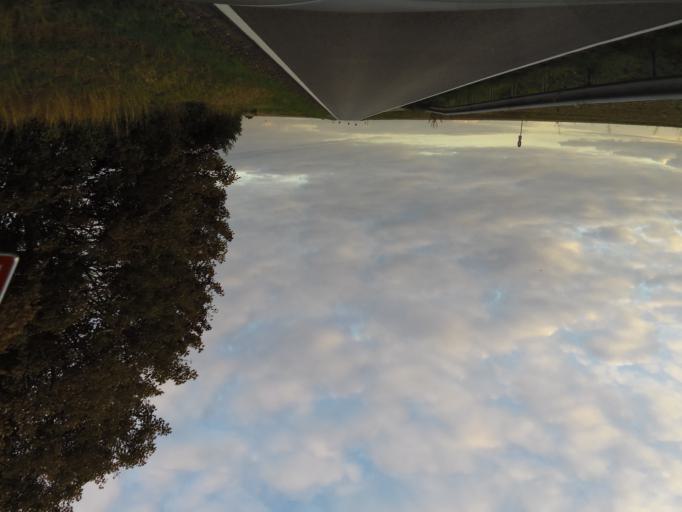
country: DE
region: Rheinland-Pfalz
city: Dalheim
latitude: 49.8365
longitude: 8.3020
